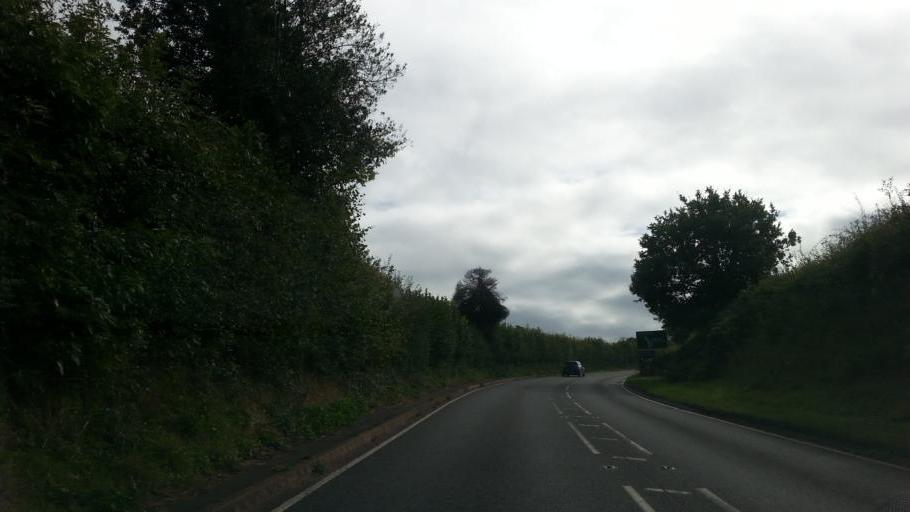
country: GB
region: England
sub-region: Herefordshire
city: Lea
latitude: 51.8983
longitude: -2.5212
